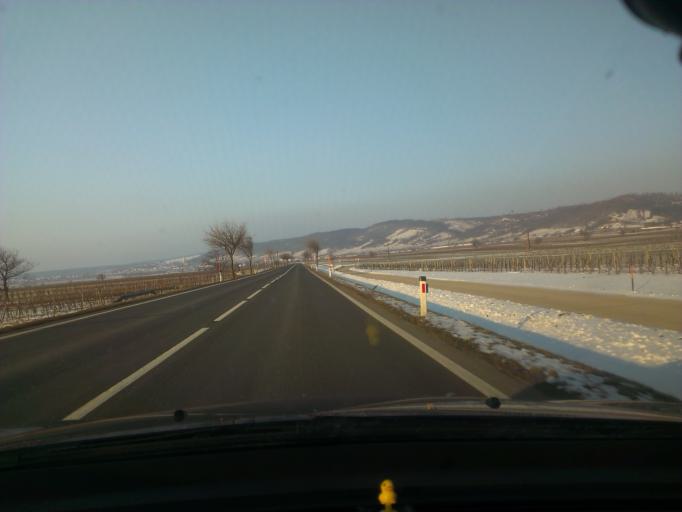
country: AT
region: Burgenland
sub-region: Eisenstadt-Umgebung
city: Donnerskirchen
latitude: 47.9098
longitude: 16.6803
